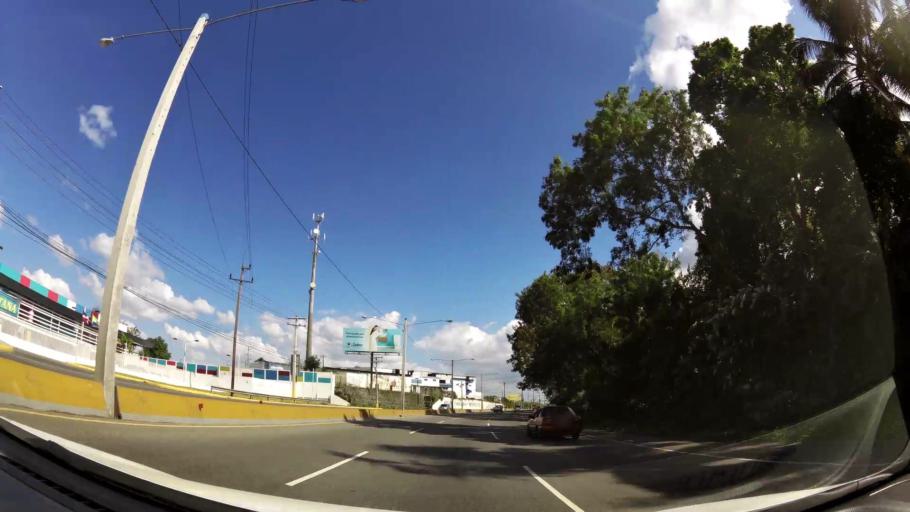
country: DO
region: Santo Domingo
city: Santo Domingo Oeste
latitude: 18.5596
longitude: -70.0598
